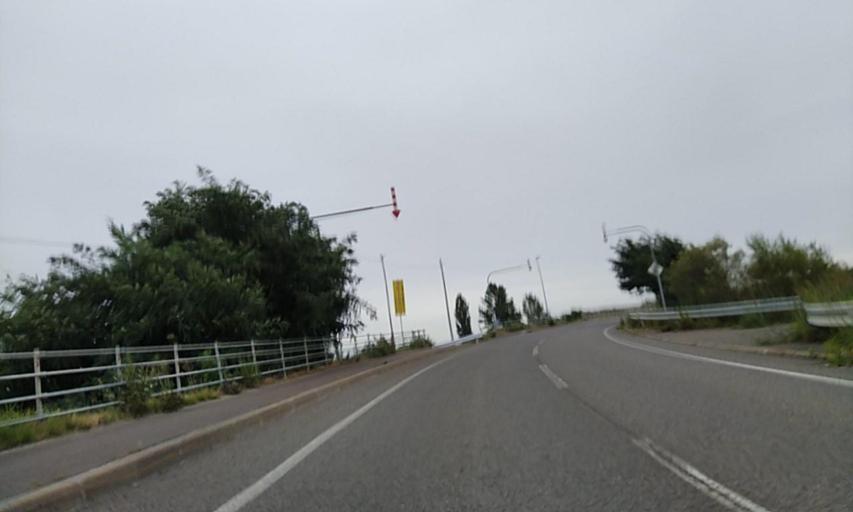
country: JP
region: Hokkaido
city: Bihoro
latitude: 43.8383
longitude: 144.1121
